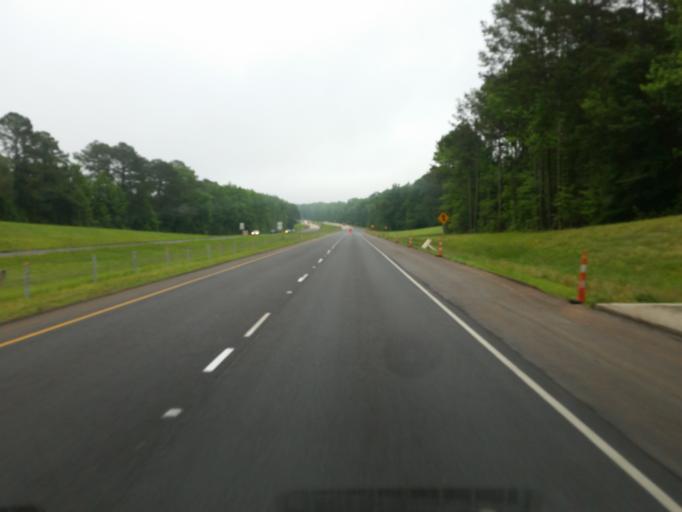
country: US
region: Louisiana
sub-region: Webster Parish
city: Minden
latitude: 32.5629
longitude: -93.1592
